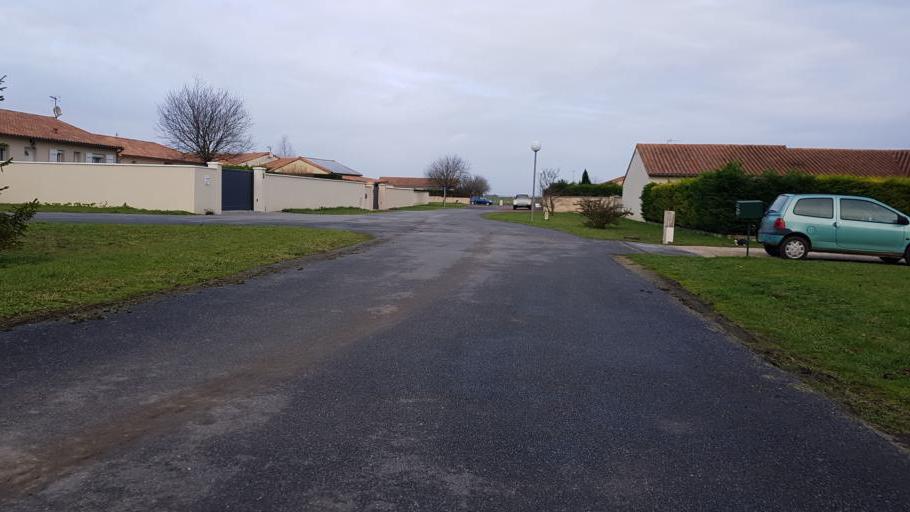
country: FR
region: Poitou-Charentes
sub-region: Departement de la Vienne
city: Avanton
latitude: 46.6636
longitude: 0.3125
